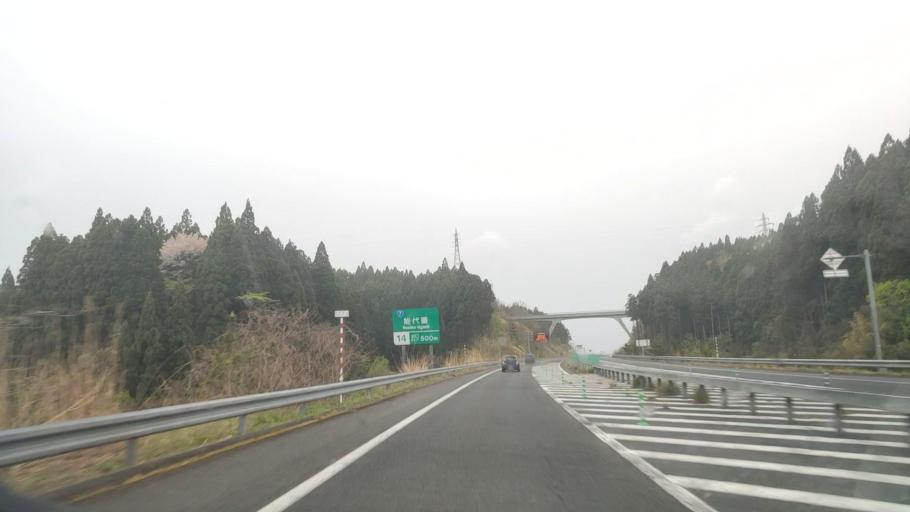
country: JP
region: Akita
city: Noshiromachi
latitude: 40.1847
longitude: 140.0914
